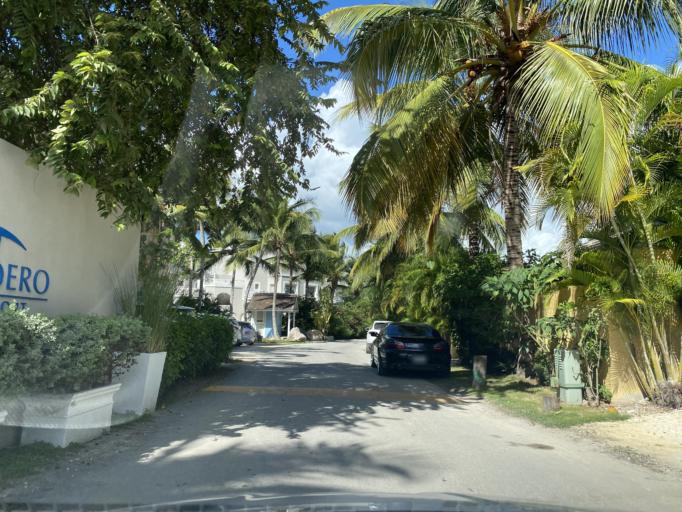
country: DO
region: La Romana
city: La Romana
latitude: 18.3511
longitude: -68.8330
